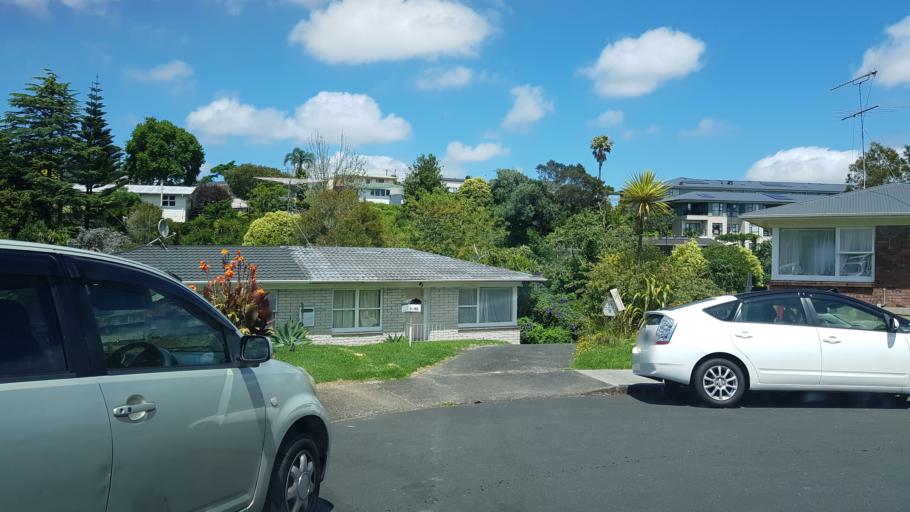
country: NZ
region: Auckland
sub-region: Auckland
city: North Shore
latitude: -36.7832
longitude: 174.7144
